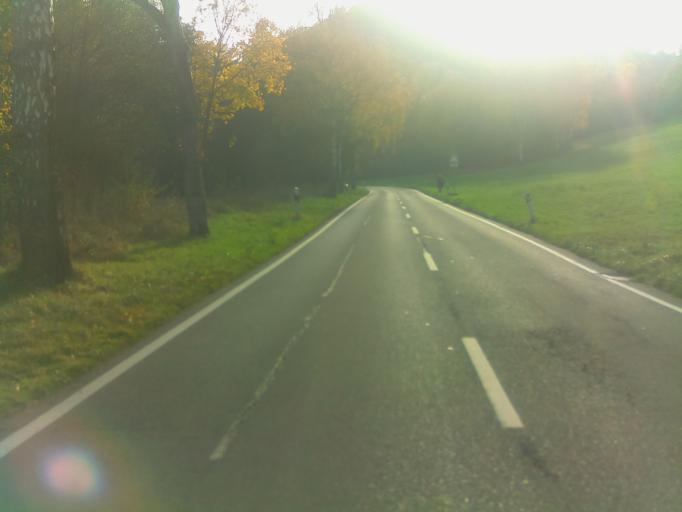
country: DE
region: Rheinland-Pfalz
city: Tiefenthal
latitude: 49.5262
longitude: 8.1049
